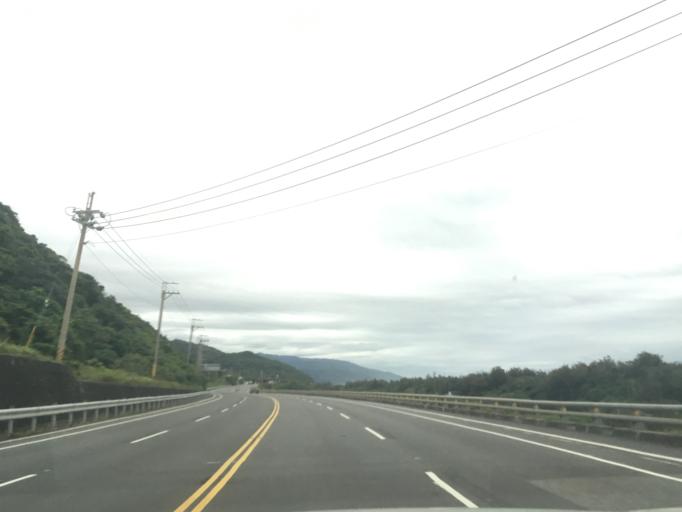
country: TW
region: Taiwan
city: Hengchun
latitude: 22.2971
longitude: 120.8887
